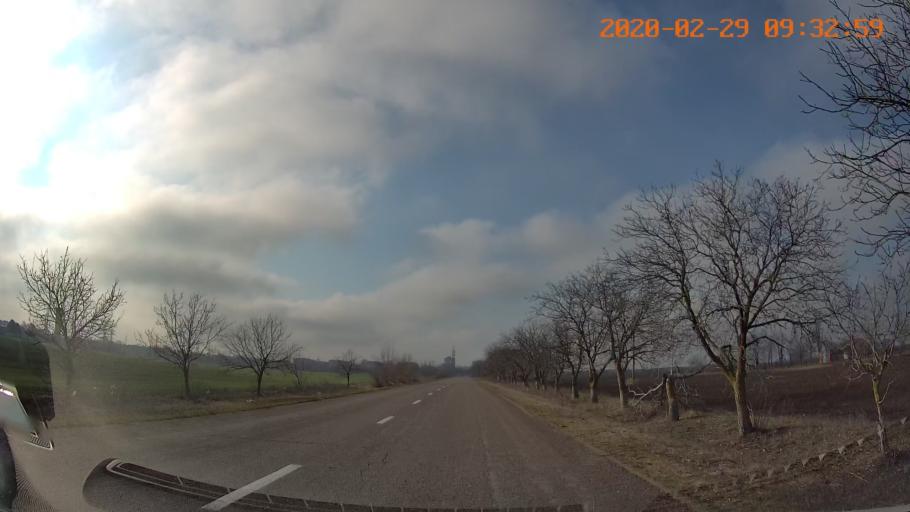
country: MD
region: Telenesti
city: Dnestrovsc
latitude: 46.6327
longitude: 29.9034
